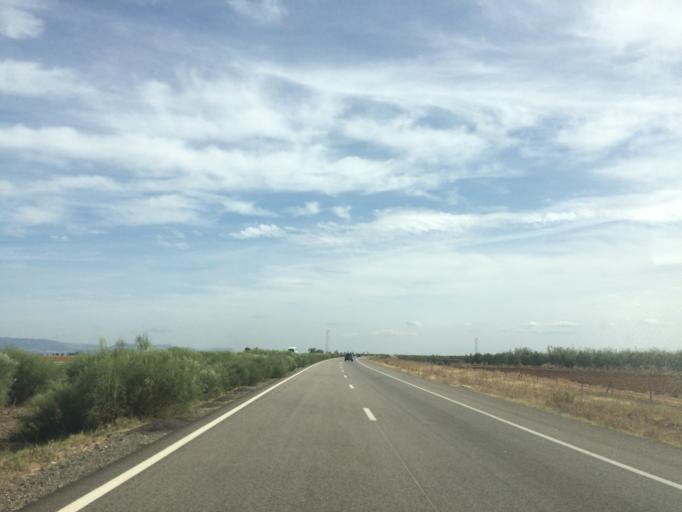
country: MA
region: Meknes-Tafilalet
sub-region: Meknes
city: Meknes
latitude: 33.8943
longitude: -5.6917
